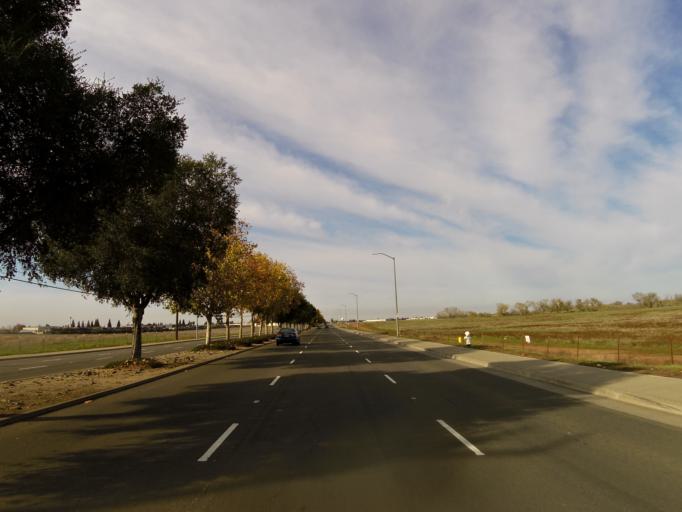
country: US
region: California
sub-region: Sacramento County
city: Rancho Cordova
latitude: 38.5627
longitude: -121.2457
